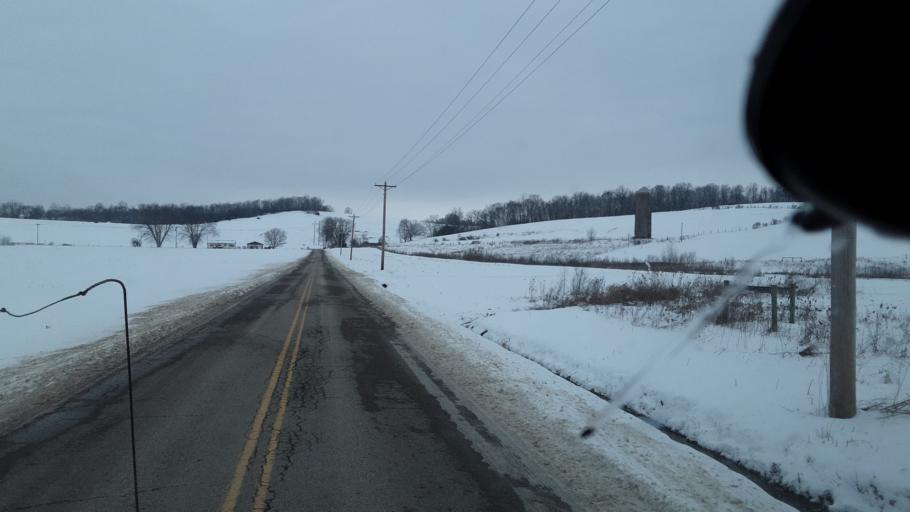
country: US
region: Ohio
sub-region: Perry County
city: Somerset
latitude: 39.8914
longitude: -82.2395
